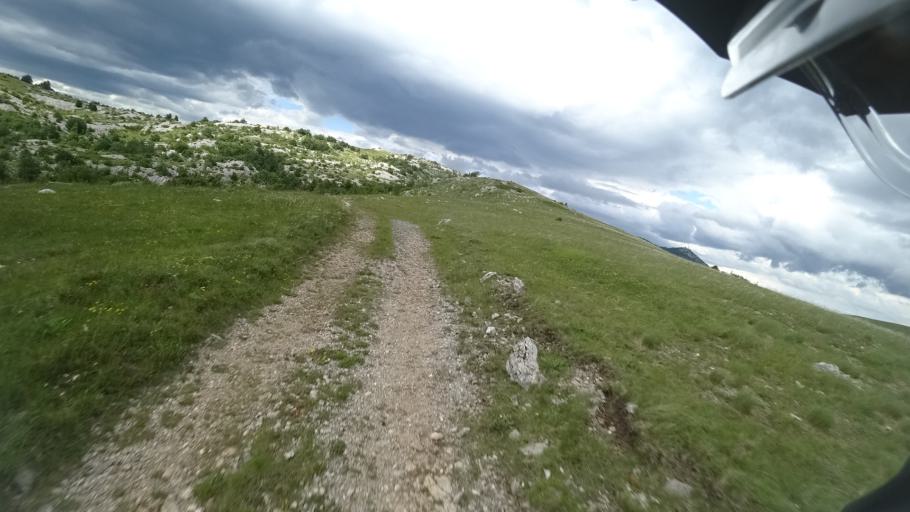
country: HR
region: Zadarska
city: Obrovac
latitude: 44.2669
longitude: 15.7366
